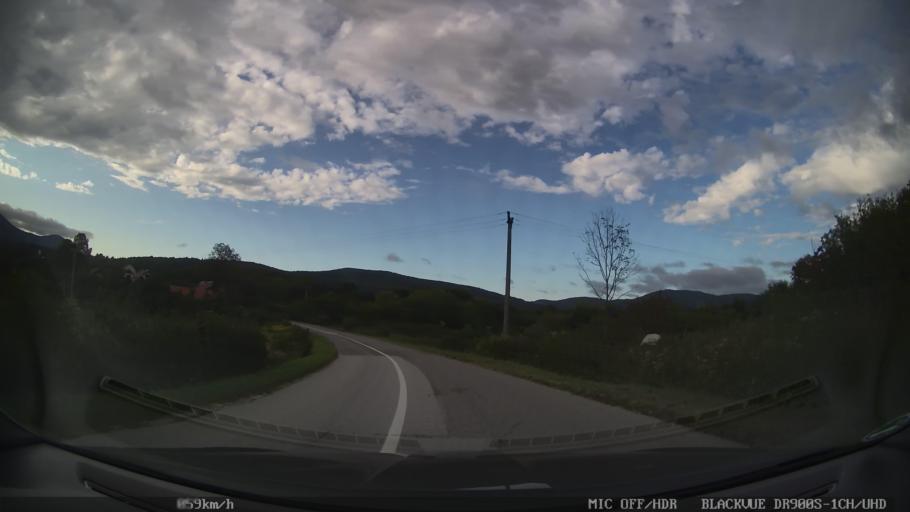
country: HR
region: Karlovacka
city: Plaski
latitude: 44.9927
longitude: 15.4476
